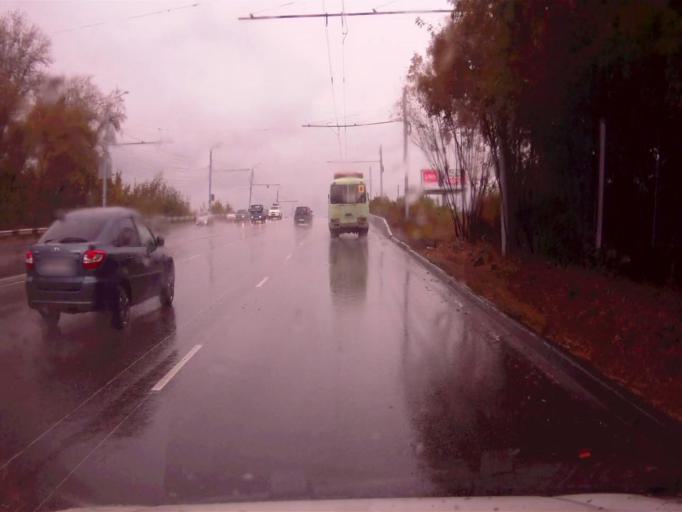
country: RU
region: Chelyabinsk
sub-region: Gorod Chelyabinsk
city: Chelyabinsk
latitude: 55.1958
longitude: 61.3862
